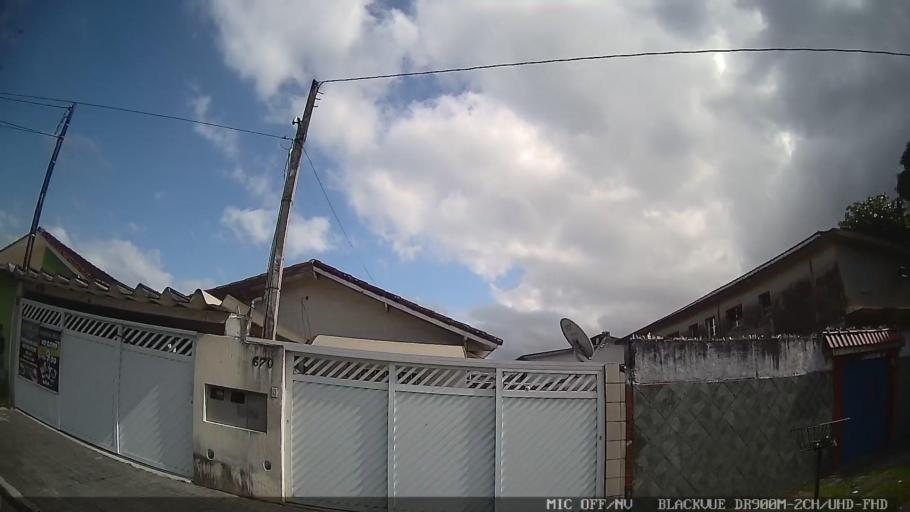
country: BR
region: Sao Paulo
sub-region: Guaruja
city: Guaruja
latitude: -23.9980
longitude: -46.2769
